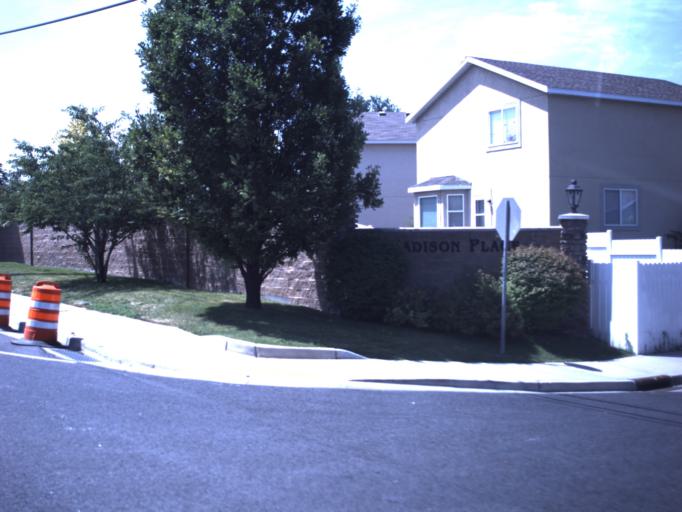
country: US
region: Utah
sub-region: Salt Lake County
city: West Valley City
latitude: 40.6861
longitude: -112.0249
